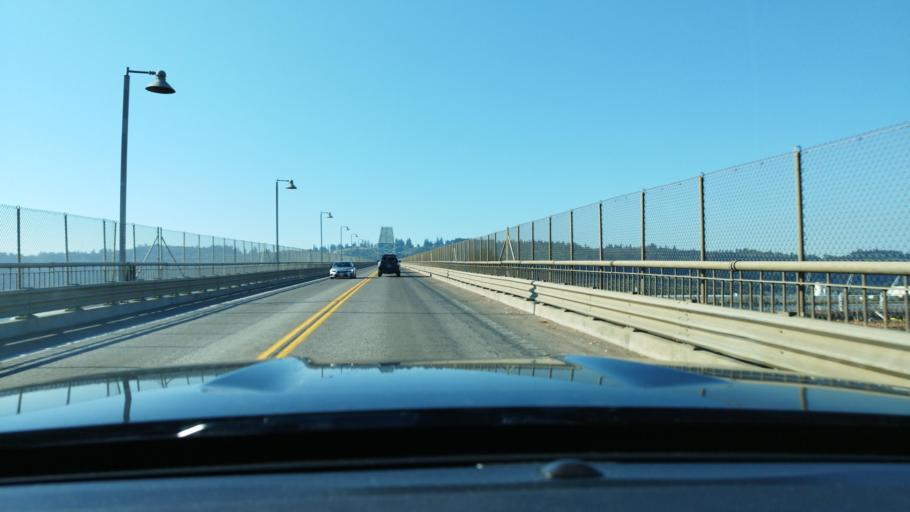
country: US
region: Oregon
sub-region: Columbia County
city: Rainier
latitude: 46.1116
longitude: -122.9538
